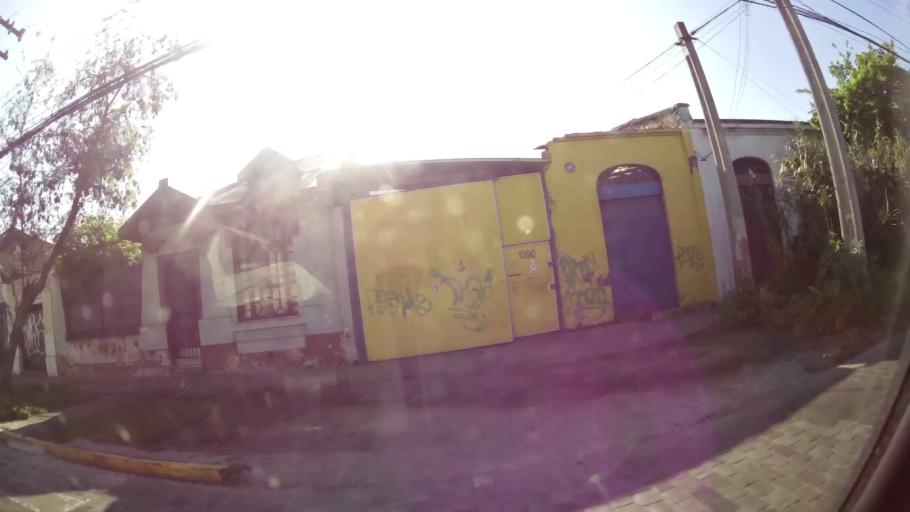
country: CL
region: Santiago Metropolitan
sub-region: Provincia de Santiago
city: Santiago
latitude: -33.4614
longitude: -70.6320
